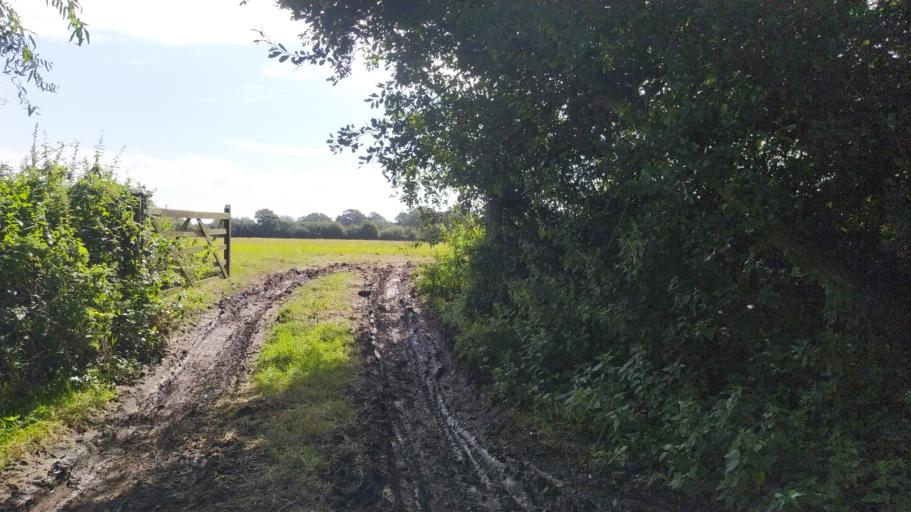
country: GB
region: England
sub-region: West Sussex
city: Chichester
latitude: 50.8107
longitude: -0.7557
